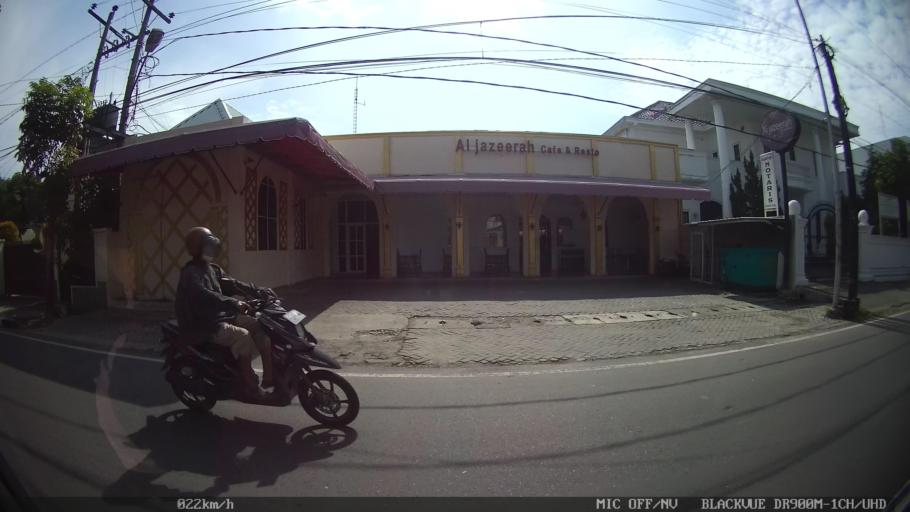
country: ID
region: North Sumatra
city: Medan
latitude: 3.5815
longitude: 98.6576
